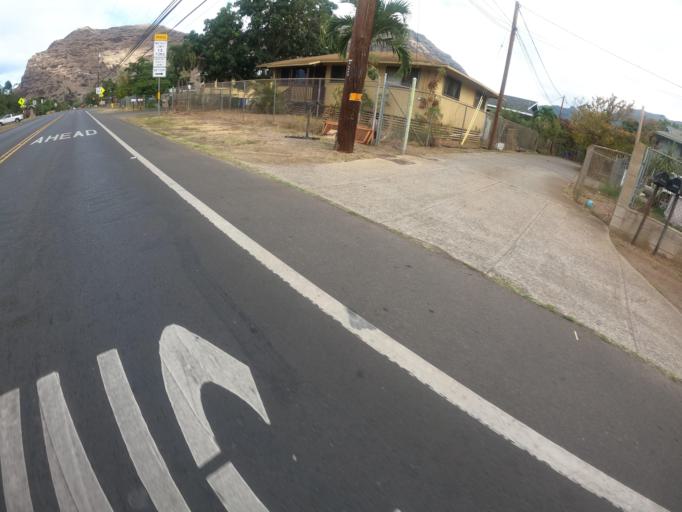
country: US
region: Hawaii
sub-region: Honolulu County
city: Makaha
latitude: 21.4714
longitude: -158.2165
